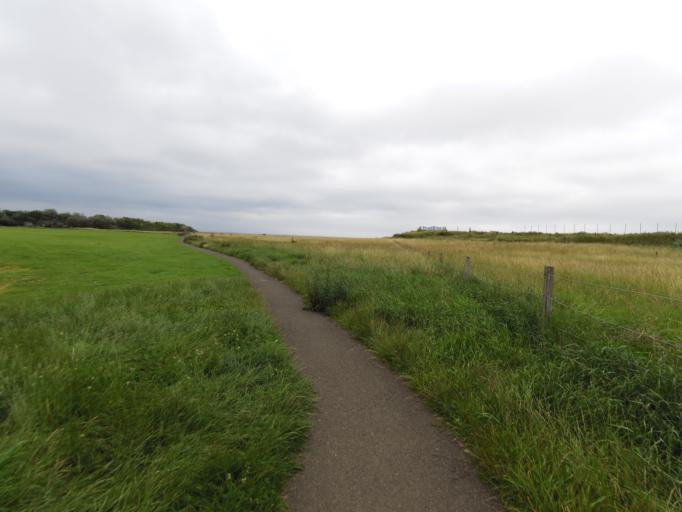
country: GB
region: Scotland
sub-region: East Lothian
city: Musselburgh
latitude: 55.9488
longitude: -3.0200
